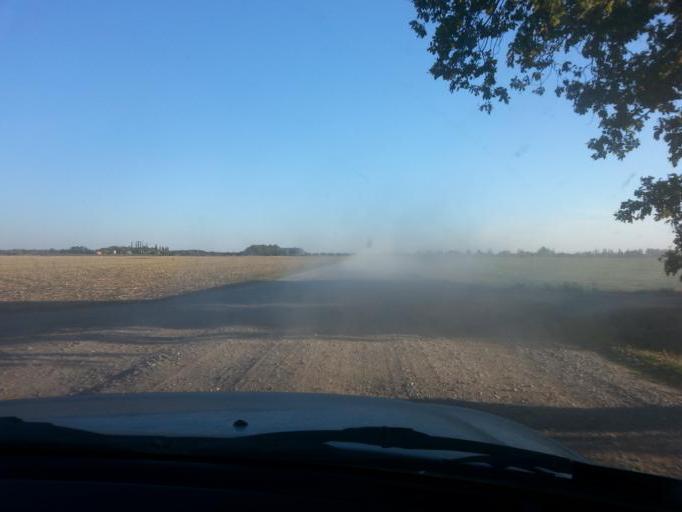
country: LV
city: Tervete
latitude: 56.6069
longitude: 23.4839
